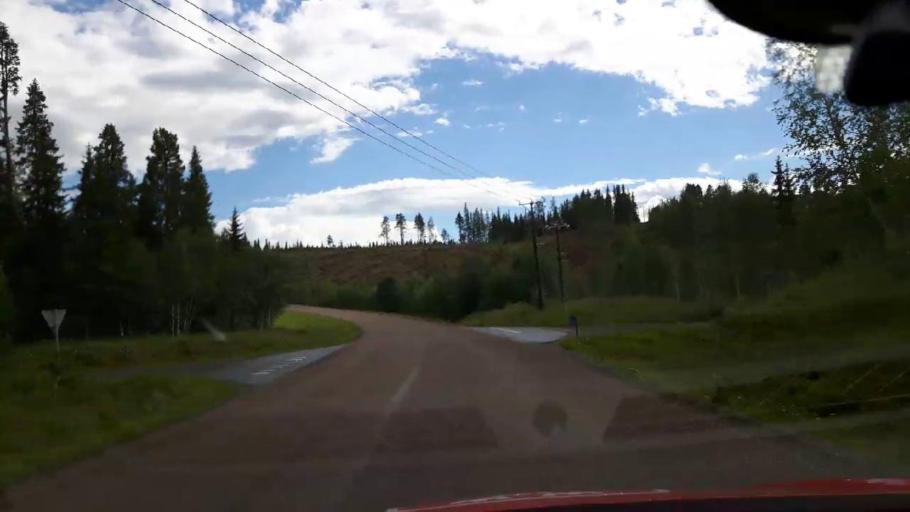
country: SE
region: Jaemtland
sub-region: Are Kommun
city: Are
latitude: 63.3025
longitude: 13.2214
